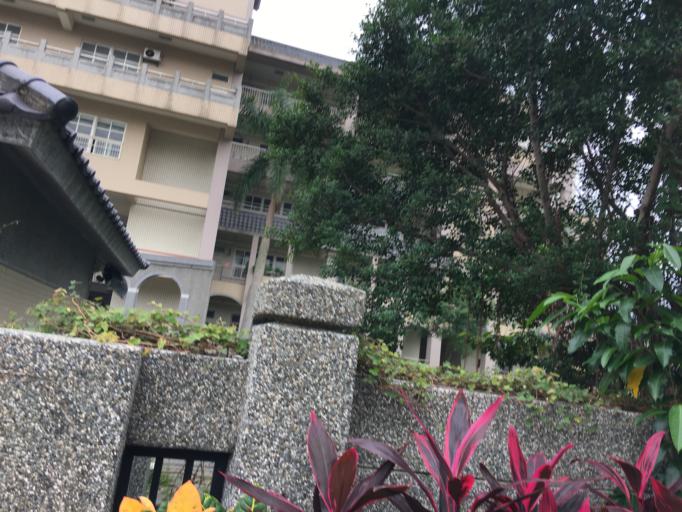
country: TW
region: Taiwan
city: Taoyuan City
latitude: 25.0182
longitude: 121.3063
